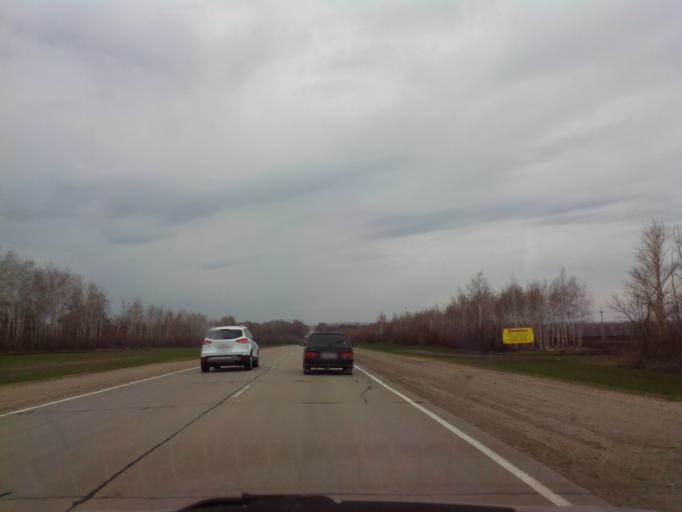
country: RU
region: Tambov
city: Znamenka
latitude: 52.3857
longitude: 41.4080
